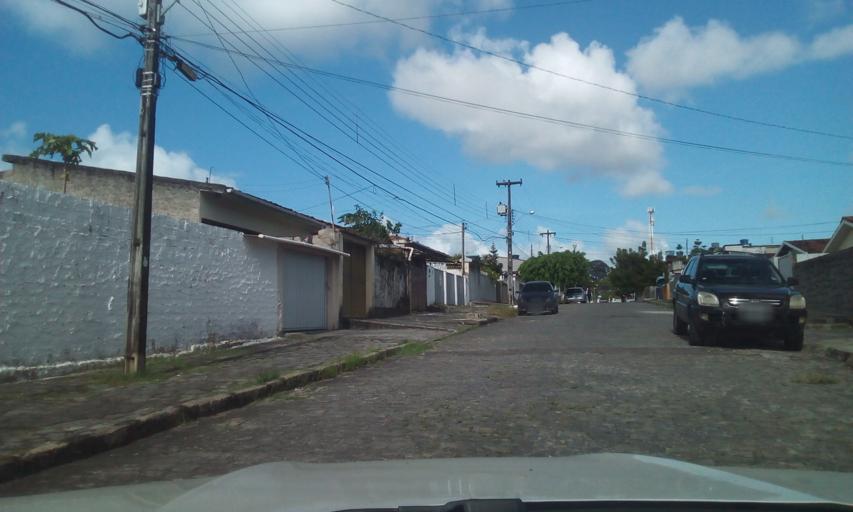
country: BR
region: Paraiba
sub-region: Joao Pessoa
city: Joao Pessoa
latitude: -7.1357
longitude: -34.8537
